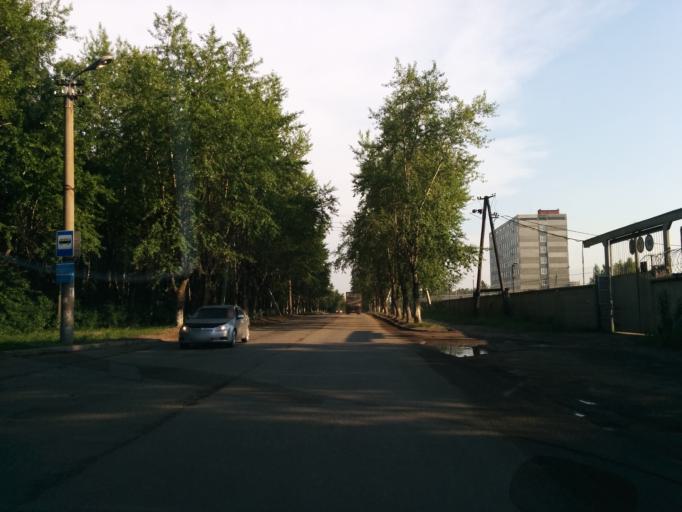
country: RU
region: Perm
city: Perm
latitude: 58.1217
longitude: 56.2928
